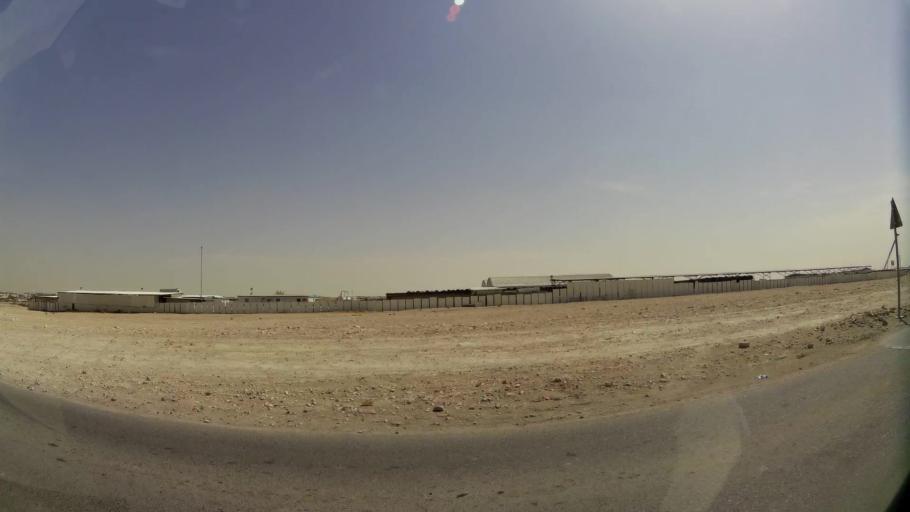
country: QA
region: Baladiyat ar Rayyan
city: Ar Rayyan
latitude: 25.2644
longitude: 51.3872
